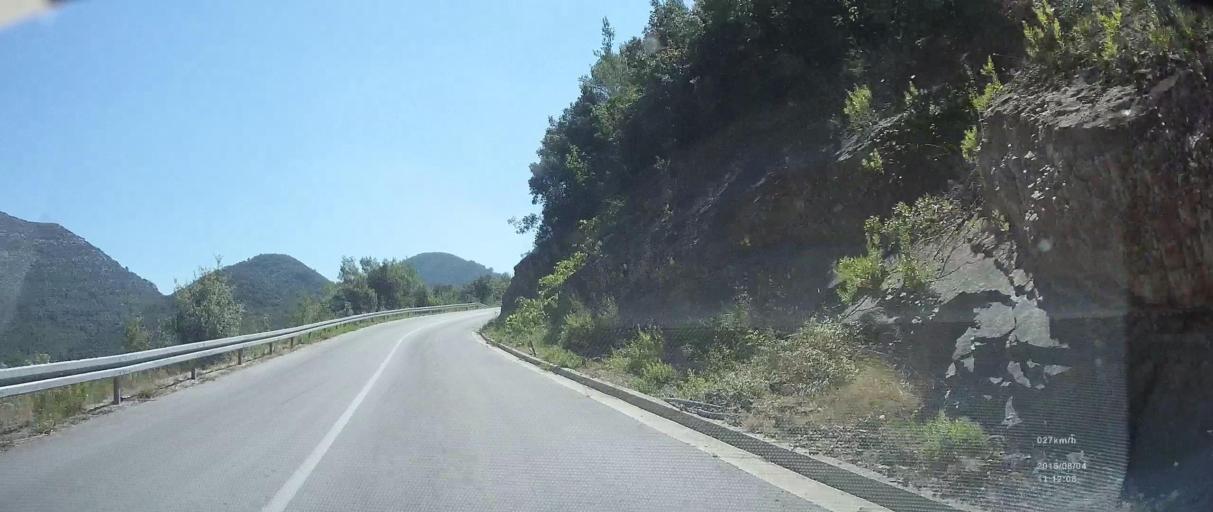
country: HR
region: Dubrovacko-Neretvanska
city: Blato
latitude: 42.7582
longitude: 17.4717
